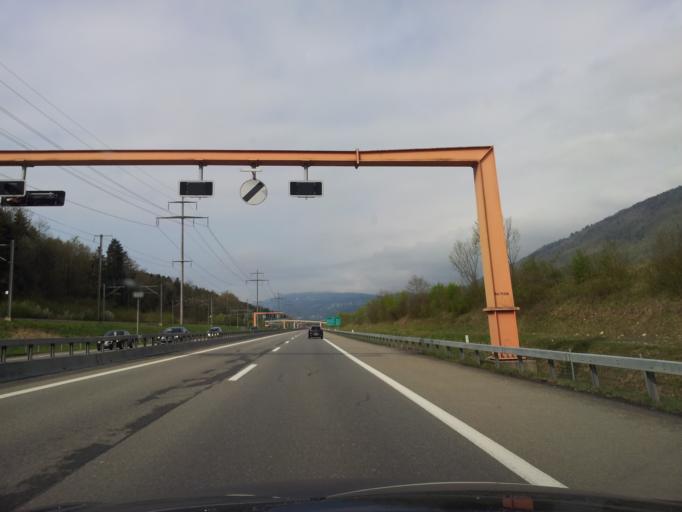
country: CH
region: Bern
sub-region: Biel/Bienne District
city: Pieterlen
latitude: 47.1675
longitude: 7.3232
